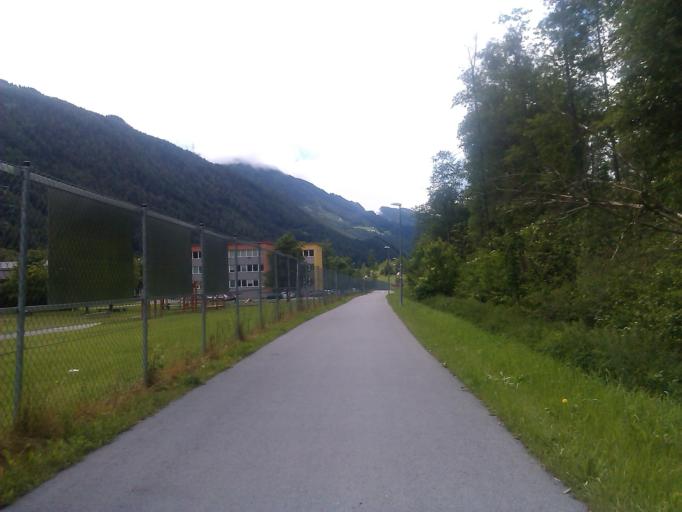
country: AT
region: Tyrol
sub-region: Politischer Bezirk Landeck
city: Fendels
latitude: 47.0657
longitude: 10.6609
